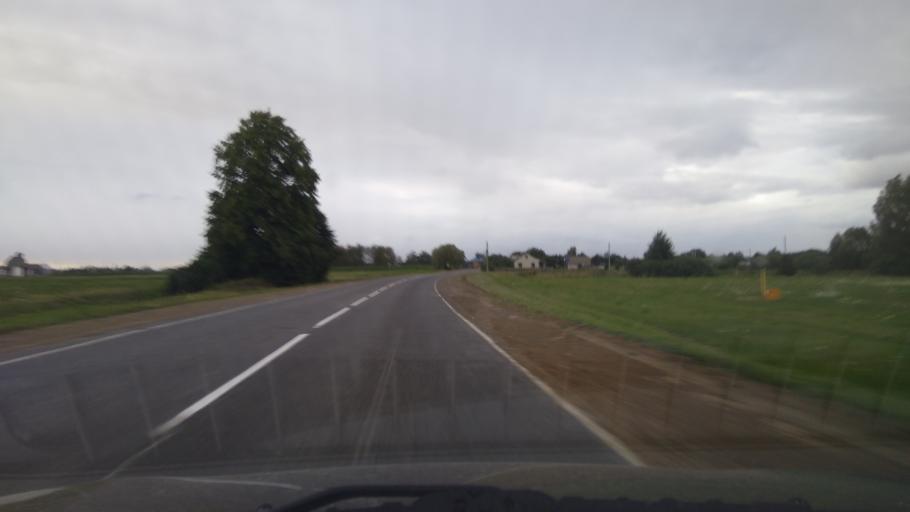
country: BY
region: Brest
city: Byaroza
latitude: 52.4507
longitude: 24.9703
